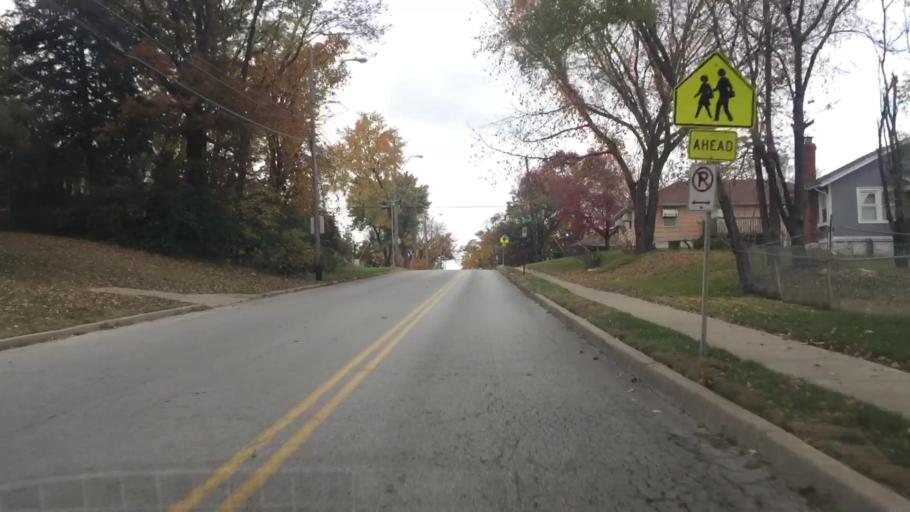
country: US
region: Kansas
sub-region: Johnson County
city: Mission Hills
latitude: 38.9949
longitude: -94.5431
